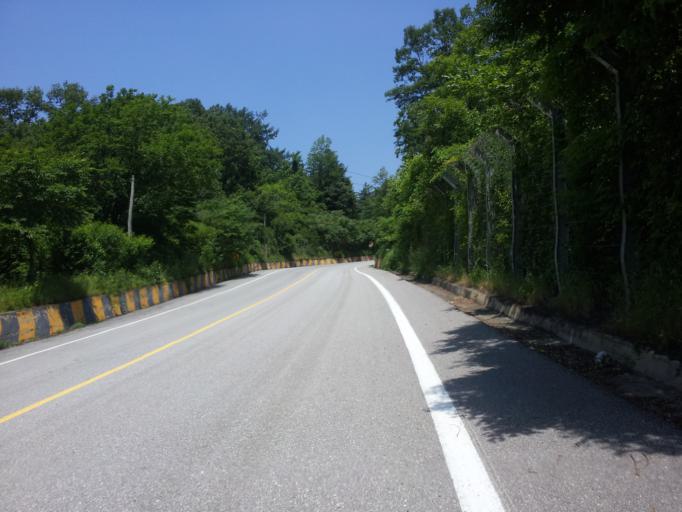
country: KR
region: Chungcheongbuk-do
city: Okcheon
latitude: 36.3551
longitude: 127.5932
